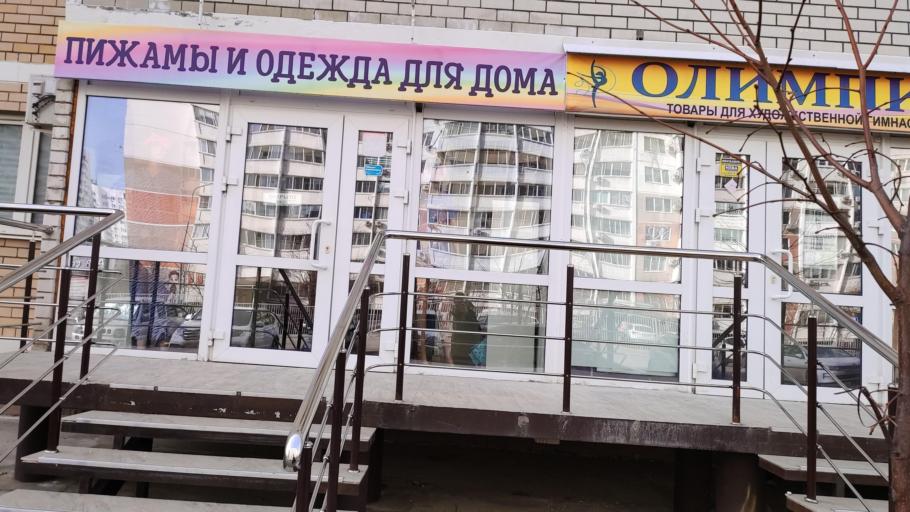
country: RU
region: Krasnodarskiy
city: Krasnodar
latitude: 45.0707
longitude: 39.0069
